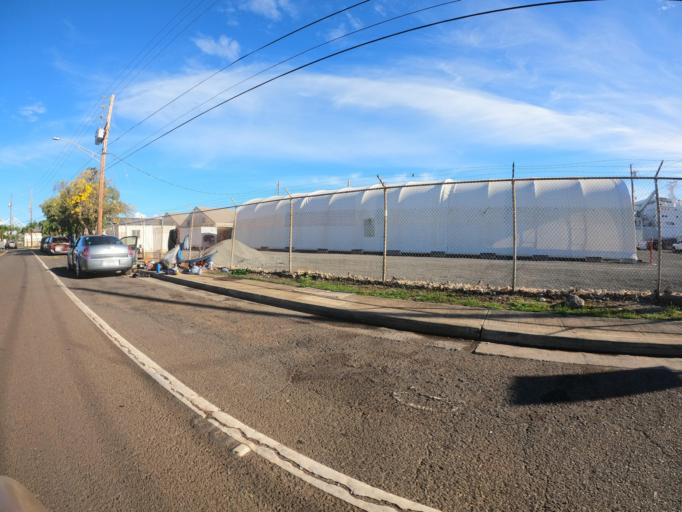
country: US
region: Hawaii
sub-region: Honolulu County
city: Honolulu
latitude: 21.3037
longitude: -157.8716
